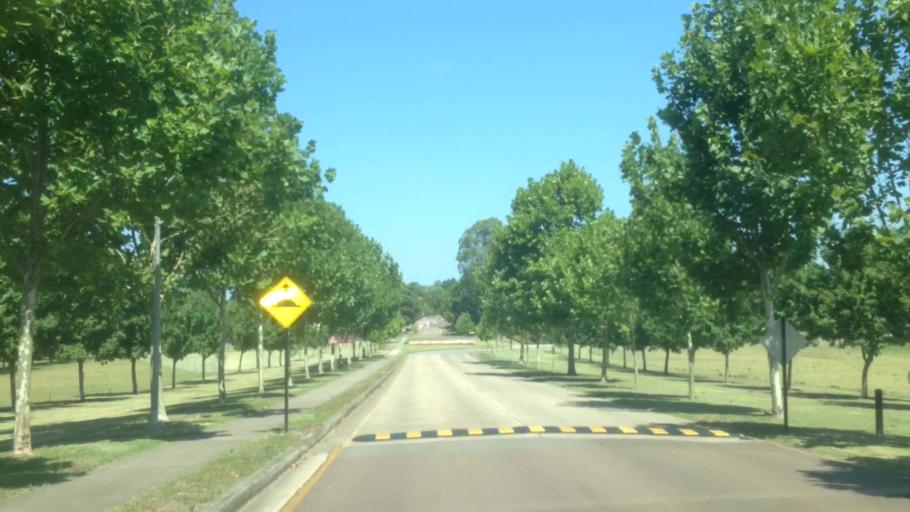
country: AU
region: New South Wales
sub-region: Lake Macquarie Shire
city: Cooranbong
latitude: -33.0837
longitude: 151.4580
